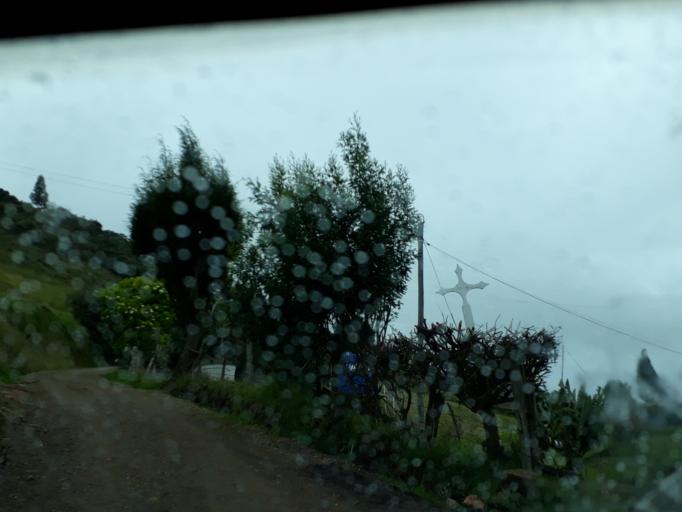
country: CO
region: Cundinamarca
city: Nemocon
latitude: 5.1538
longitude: -73.9040
